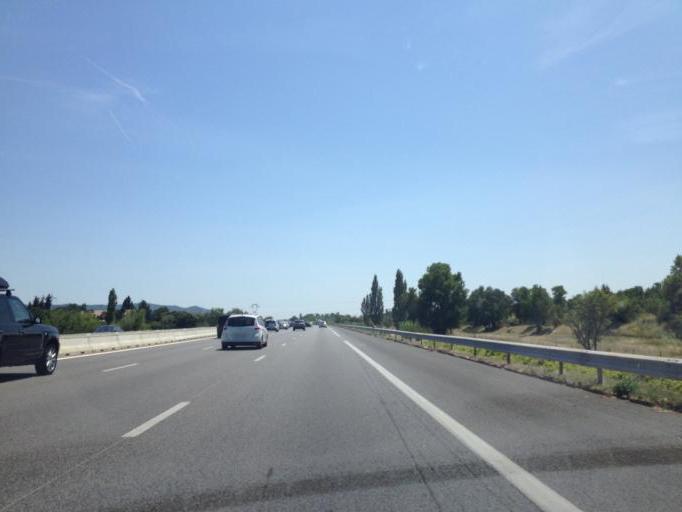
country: FR
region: Rhone-Alpes
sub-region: Departement de la Drome
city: Pierrelatte
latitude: 44.3773
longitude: 4.7323
